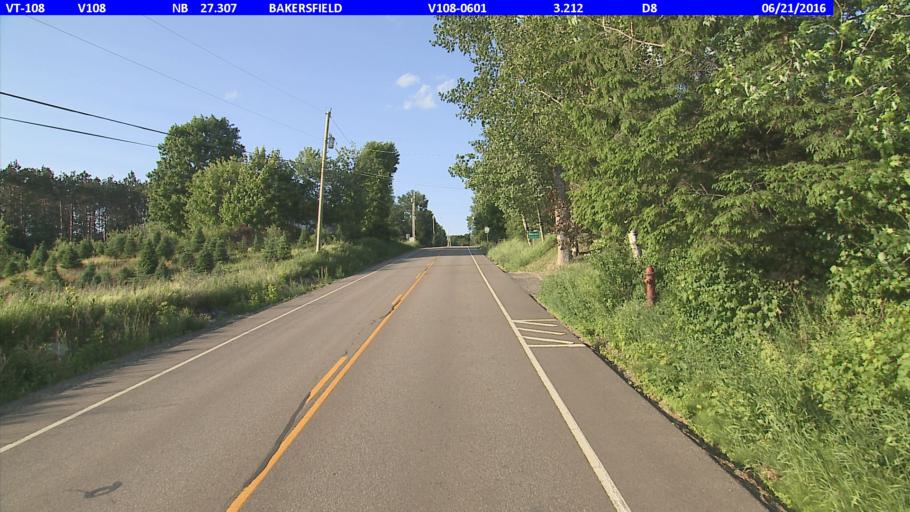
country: US
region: Vermont
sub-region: Franklin County
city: Enosburg Falls
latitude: 44.7759
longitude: -72.8050
